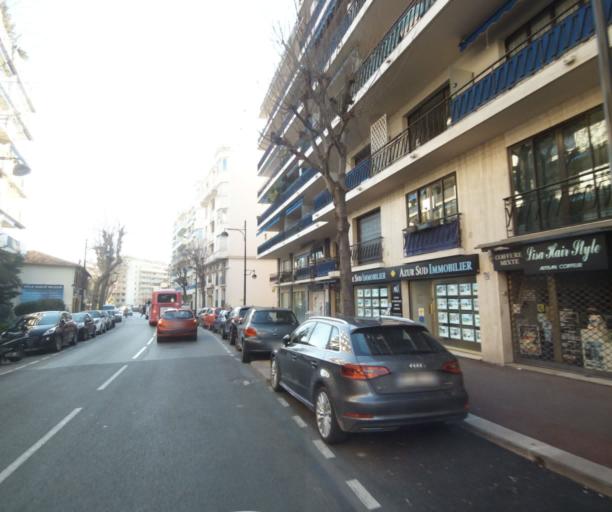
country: FR
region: Provence-Alpes-Cote d'Azur
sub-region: Departement des Alpes-Maritimes
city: Antibes
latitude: 43.5707
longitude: 7.1143
